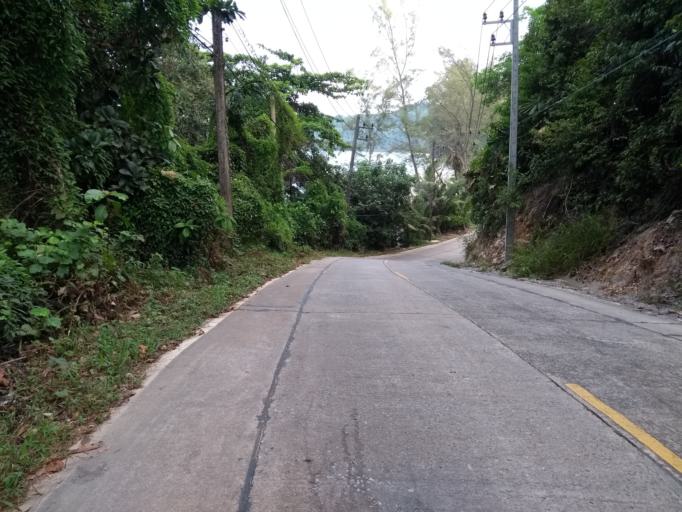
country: TH
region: Trat
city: Ko Kut
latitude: 11.6302
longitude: 102.5457
